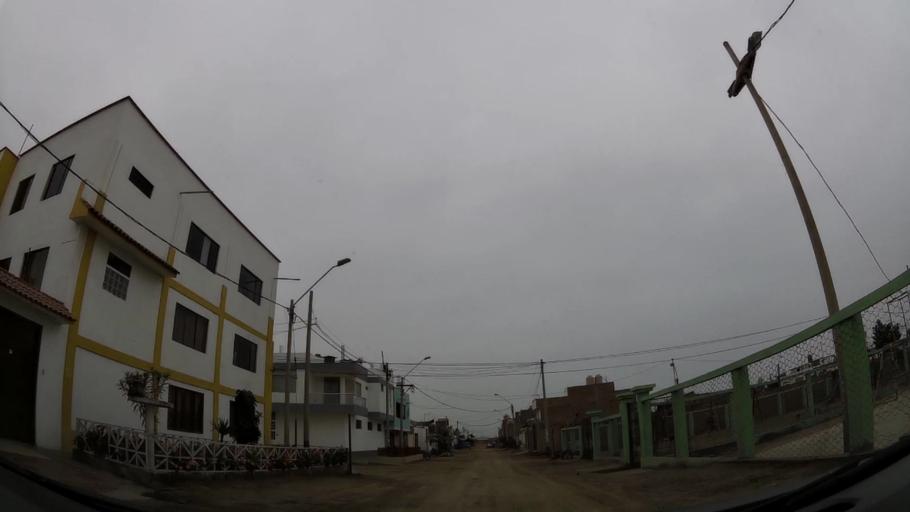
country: PE
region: Lima
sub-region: Lima
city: Punta Hermosa
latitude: -12.3168
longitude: -76.8331
